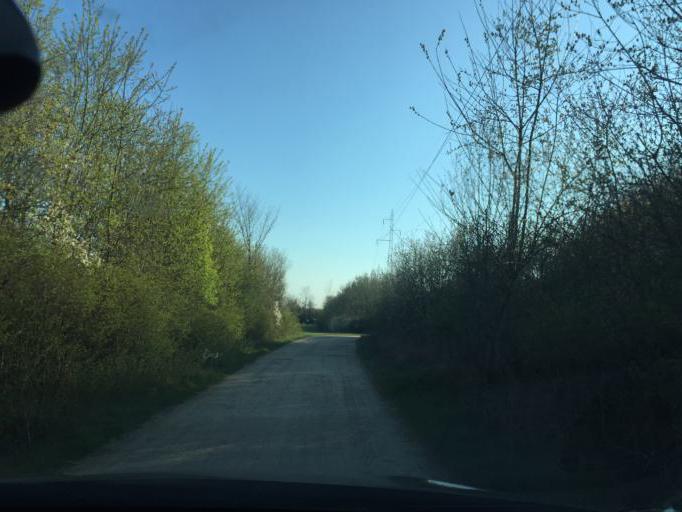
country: DK
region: South Denmark
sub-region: Odense Kommune
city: Bellinge
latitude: 55.3516
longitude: 10.3316
